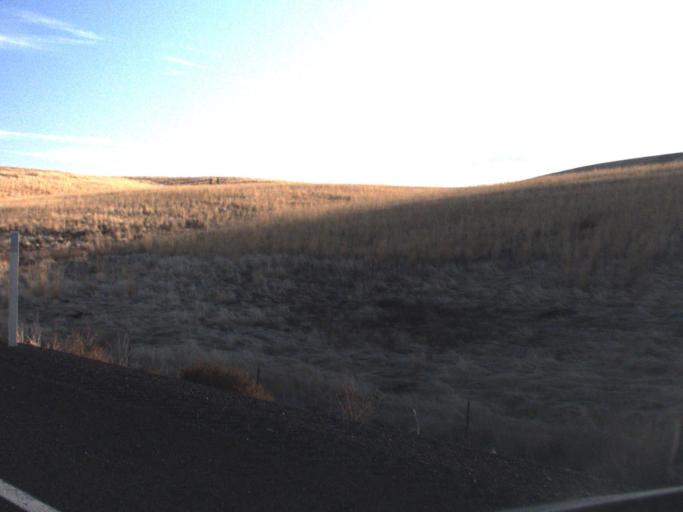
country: US
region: Washington
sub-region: Garfield County
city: Pomeroy
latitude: 46.6895
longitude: -117.7939
